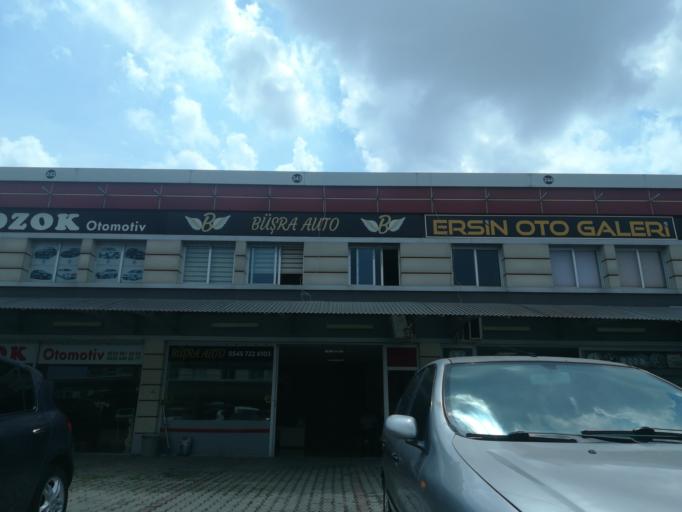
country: TR
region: Adana
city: Seyhan
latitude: 37.0014
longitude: 35.2428
